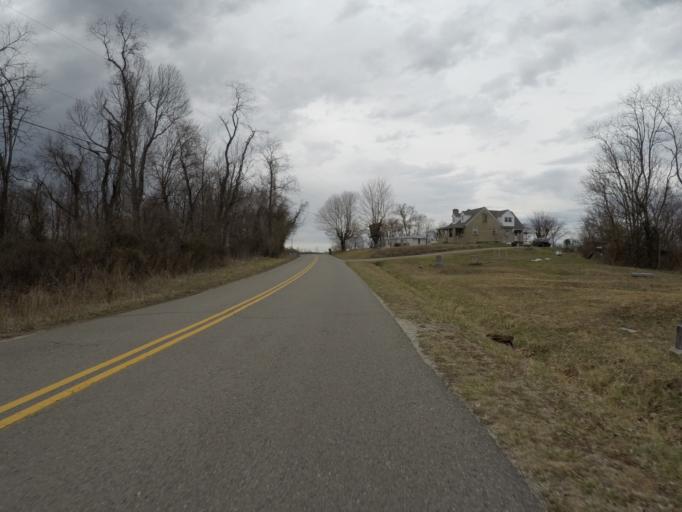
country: US
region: Ohio
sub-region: Lawrence County
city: Burlington
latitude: 38.4423
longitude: -82.5245
